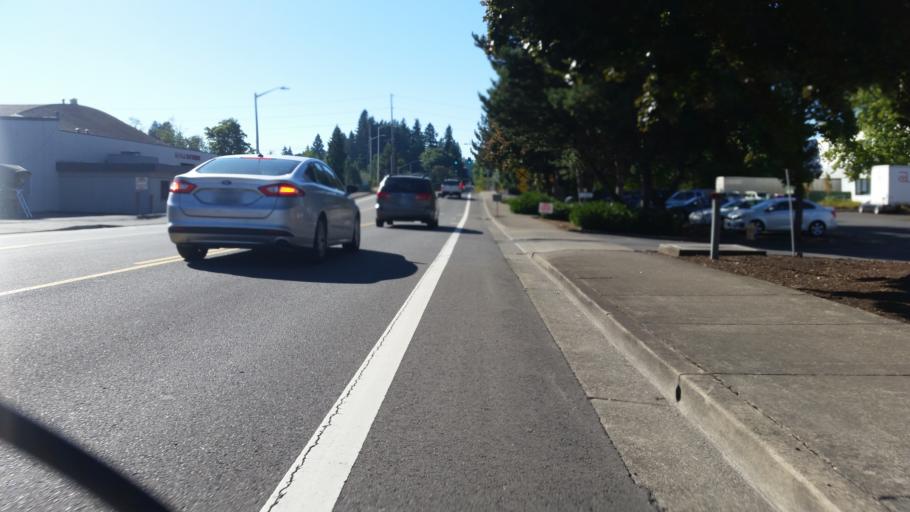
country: US
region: Oregon
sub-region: Washington County
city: Durham
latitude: 45.4153
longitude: -122.7505
